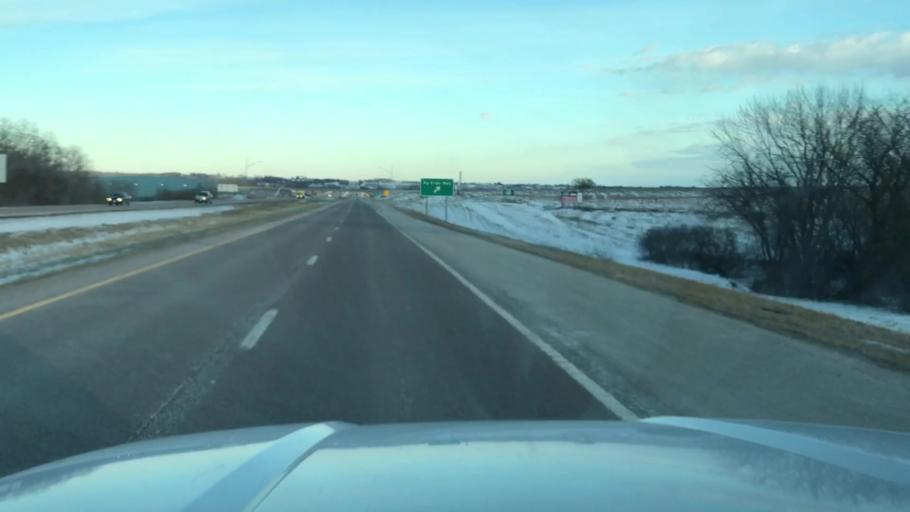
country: US
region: Missouri
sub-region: Buchanan County
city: Saint Joseph
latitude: 39.7480
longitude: -94.7590
